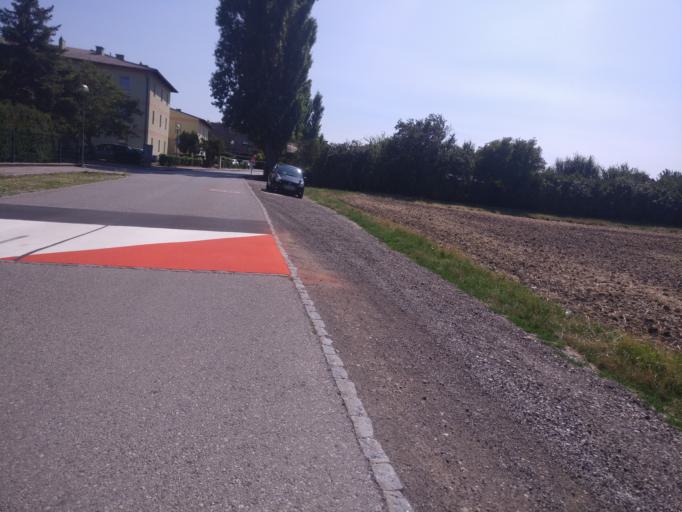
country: AT
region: Lower Austria
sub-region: Politischer Bezirk Modling
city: Guntramsdorf
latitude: 48.0304
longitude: 16.3066
